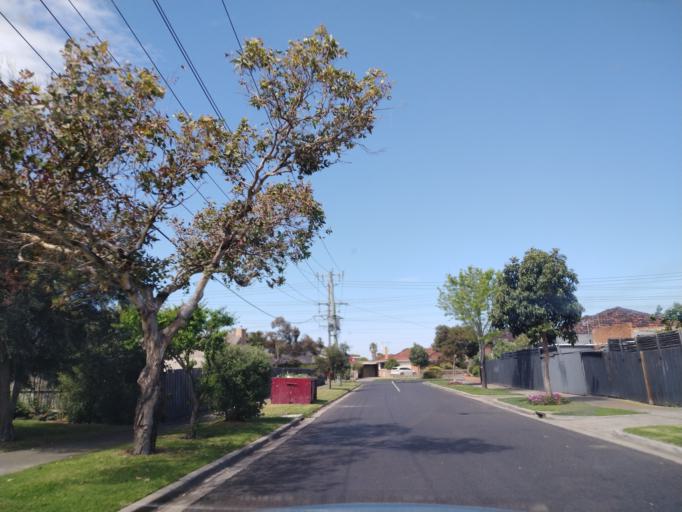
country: AU
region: Victoria
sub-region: Hobsons Bay
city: Altona North
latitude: -37.8309
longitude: 144.8519
